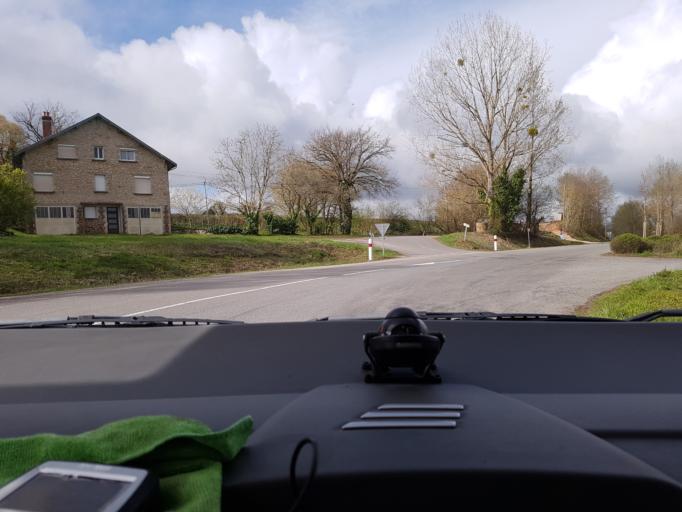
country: FR
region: Midi-Pyrenees
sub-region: Departement de l'Aveyron
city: Moyrazes
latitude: 44.3802
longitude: 2.4520
